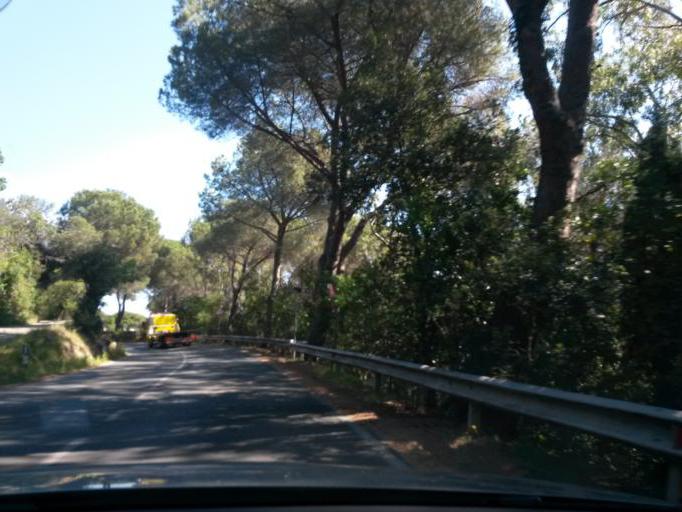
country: IT
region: Tuscany
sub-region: Provincia di Livorno
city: Marciana Marina
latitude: 42.8018
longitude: 10.2100
